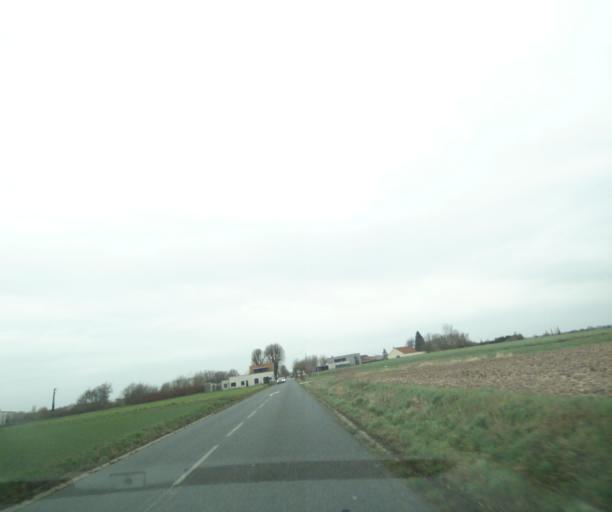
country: FR
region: Nord-Pas-de-Calais
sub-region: Departement du Nord
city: Quarouble
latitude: 50.3776
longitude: 3.6301
